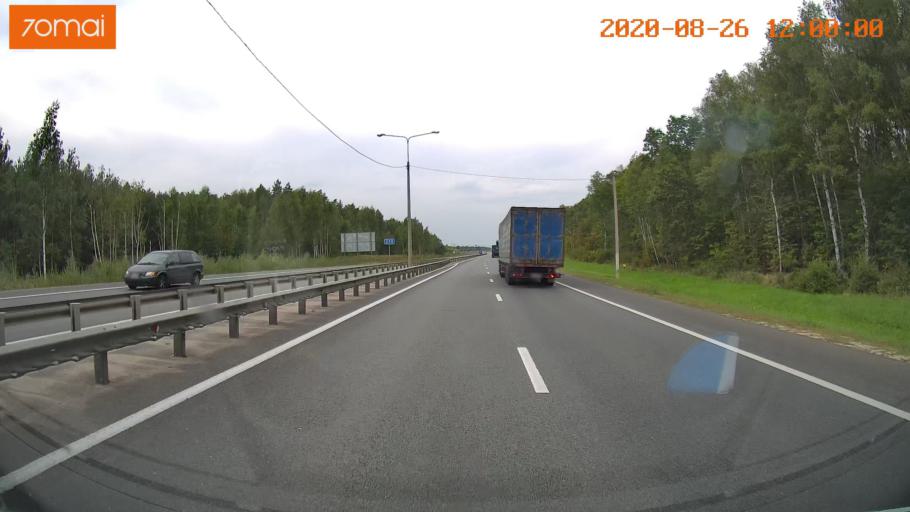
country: RU
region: Rjazan
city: Kiritsy
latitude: 54.2863
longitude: 40.2844
